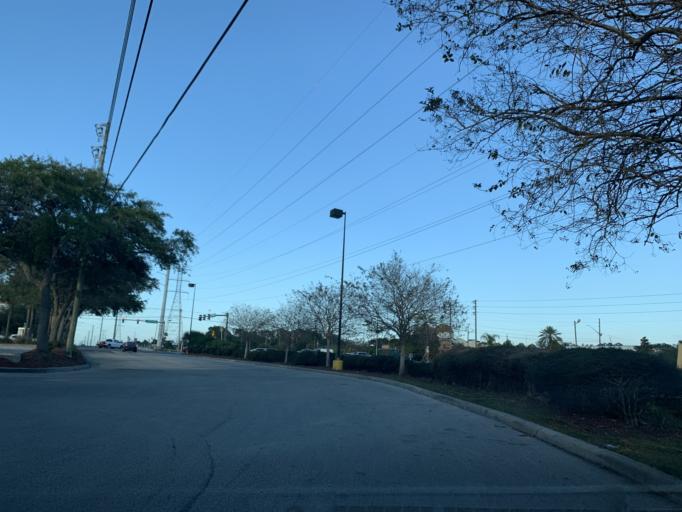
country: US
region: Florida
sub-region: Pinellas County
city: South Highpoint
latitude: 27.9596
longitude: -82.7341
